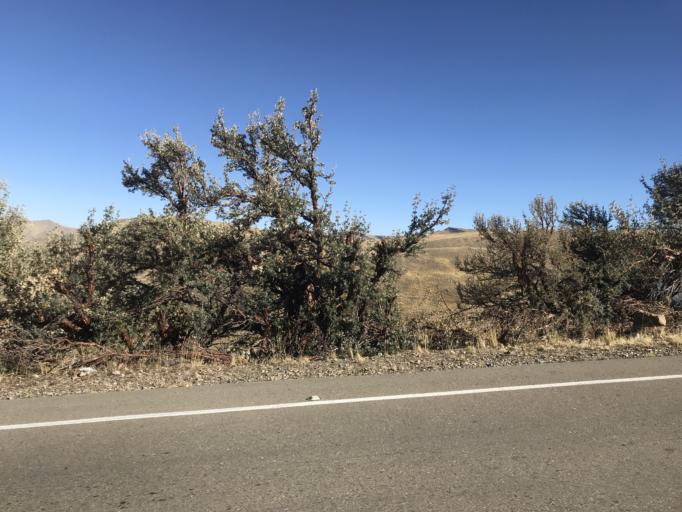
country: PE
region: Puno
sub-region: Yunguyo
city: Yunguyo
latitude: -16.1743
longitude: -68.9828
